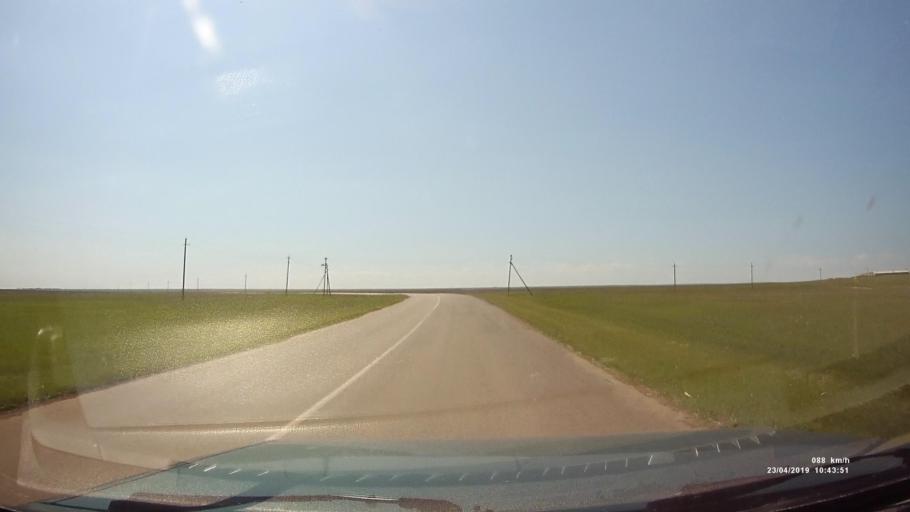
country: RU
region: Kalmykiya
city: Yashalta
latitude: 46.4650
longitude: 42.6502
